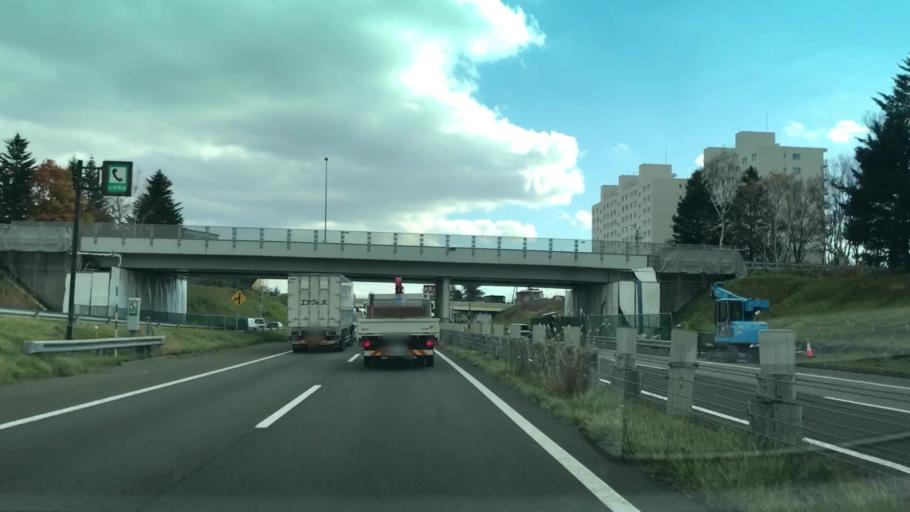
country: JP
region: Hokkaido
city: Kitahiroshima
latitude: 42.9772
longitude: 141.4780
